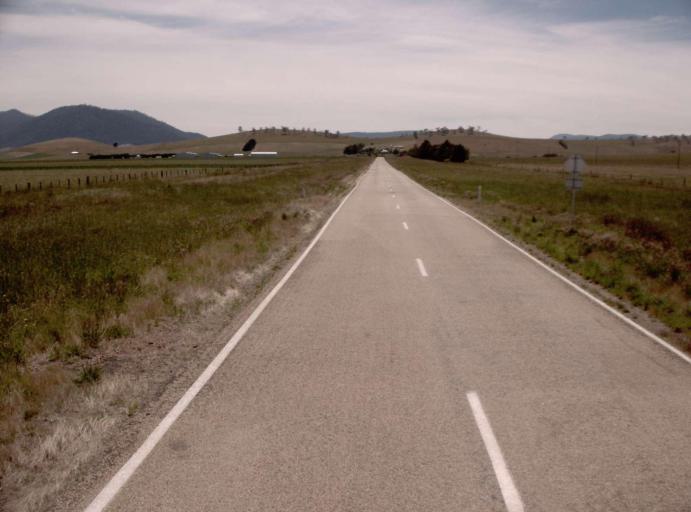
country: AU
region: Victoria
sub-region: Alpine
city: Mount Beauty
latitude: -36.9772
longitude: 147.6934
